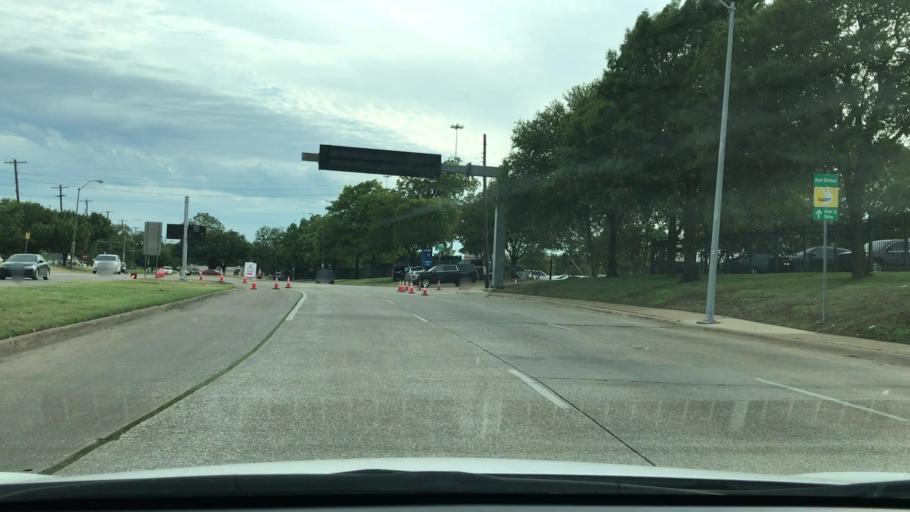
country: US
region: Texas
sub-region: Dallas County
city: Dallas
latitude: 32.7772
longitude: -96.7517
